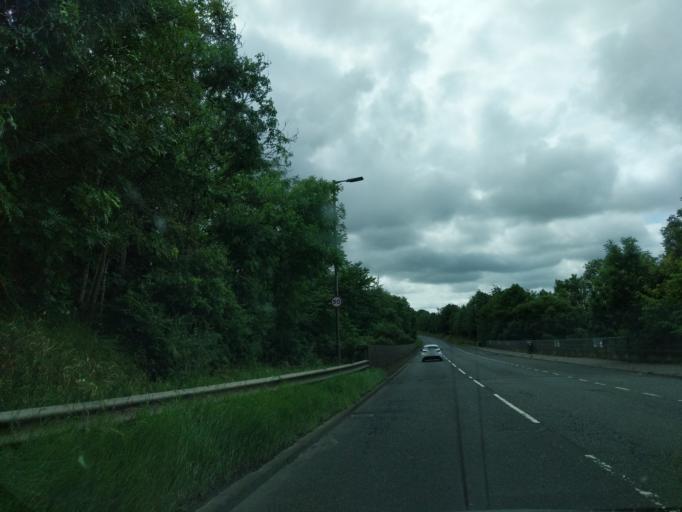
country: GB
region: Scotland
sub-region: South Lanarkshire
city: Larkhall
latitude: 55.7062
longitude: -3.9650
